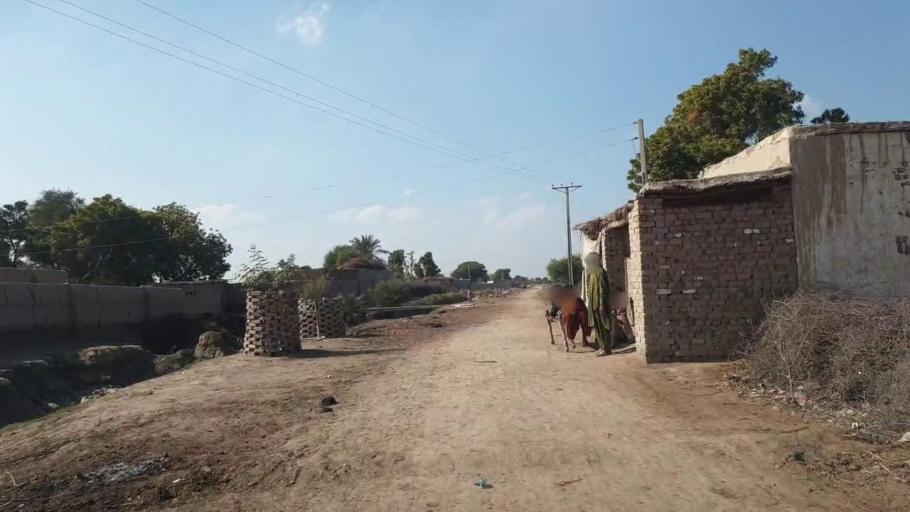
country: PK
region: Sindh
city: Shahpur Chakar
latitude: 26.0844
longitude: 68.5652
